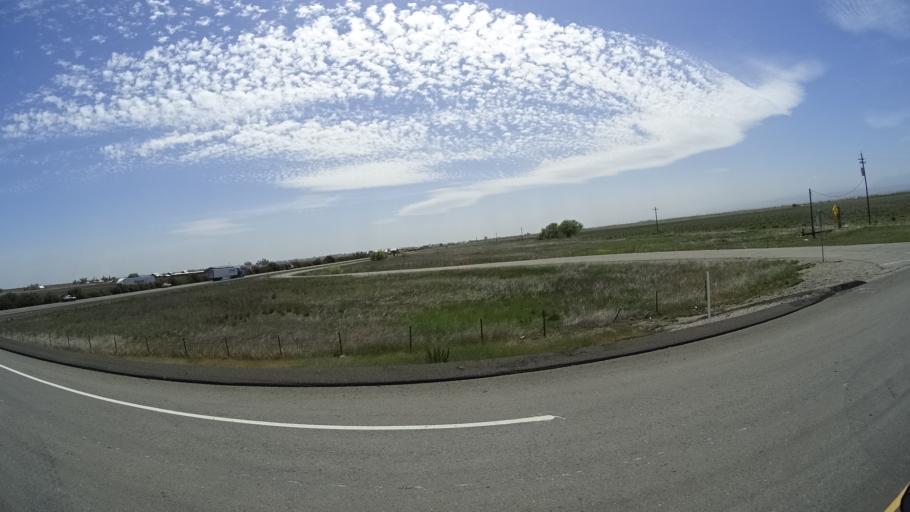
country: US
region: California
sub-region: Glenn County
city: Willows
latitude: 39.5822
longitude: -122.2120
